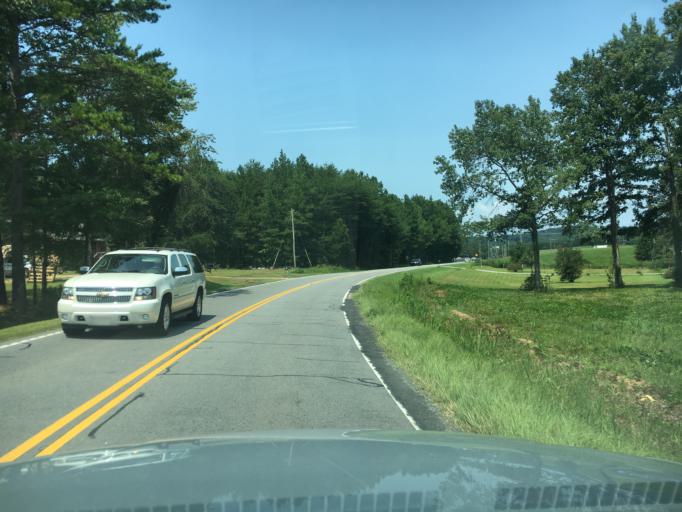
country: US
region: South Carolina
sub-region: Pickens County
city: Central
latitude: 34.6954
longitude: -82.7488
